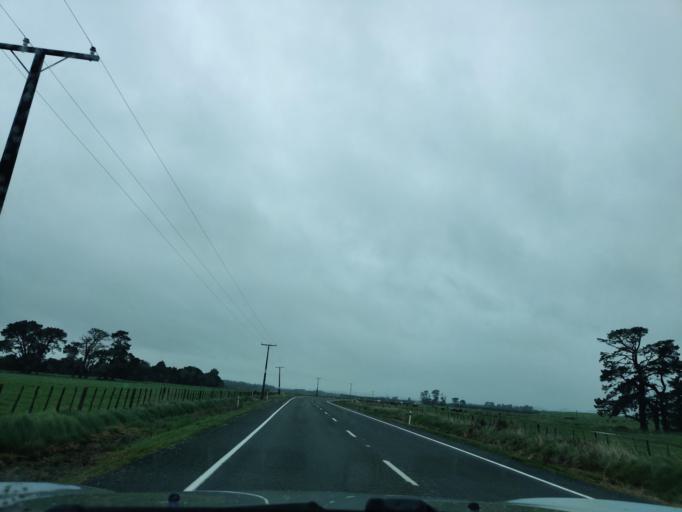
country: NZ
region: Hawke's Bay
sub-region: Hastings District
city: Hastings
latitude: -40.0200
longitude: 176.2734
